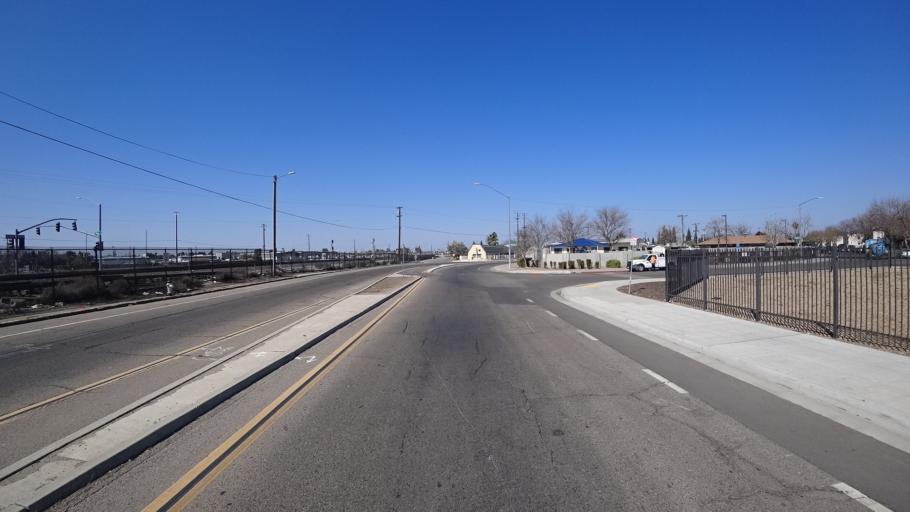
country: US
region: California
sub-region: Fresno County
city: Fresno
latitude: 36.7622
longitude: -119.8260
